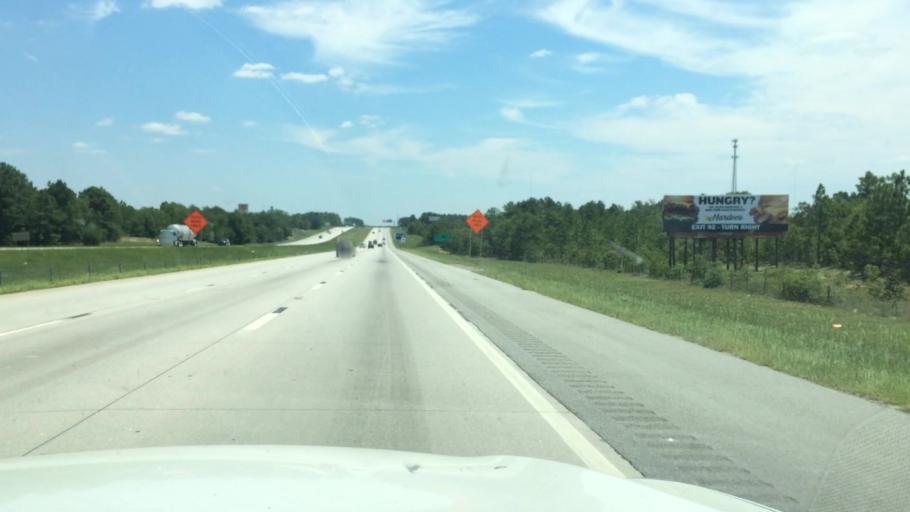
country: US
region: South Carolina
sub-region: Kershaw County
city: Elgin
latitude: 34.0996
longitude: -80.8430
